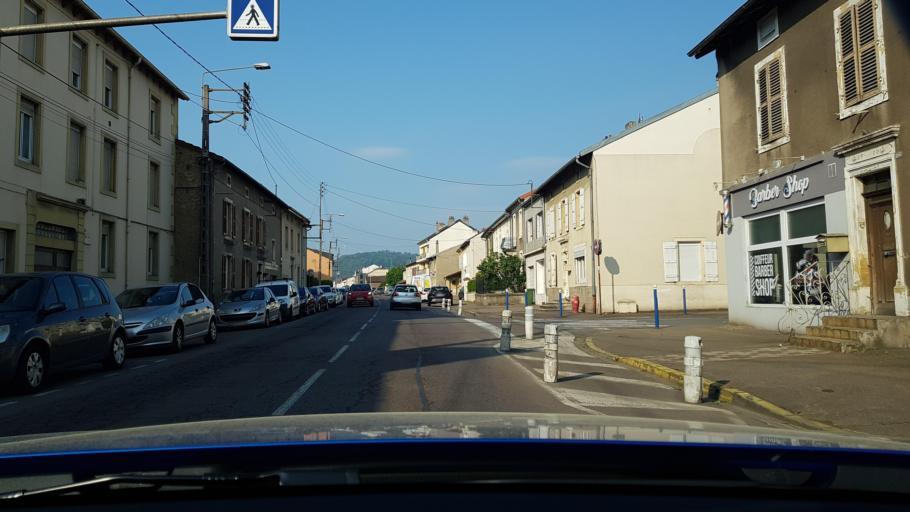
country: FR
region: Lorraine
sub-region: Departement de la Moselle
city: Florange
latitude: 49.3253
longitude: 6.1188
